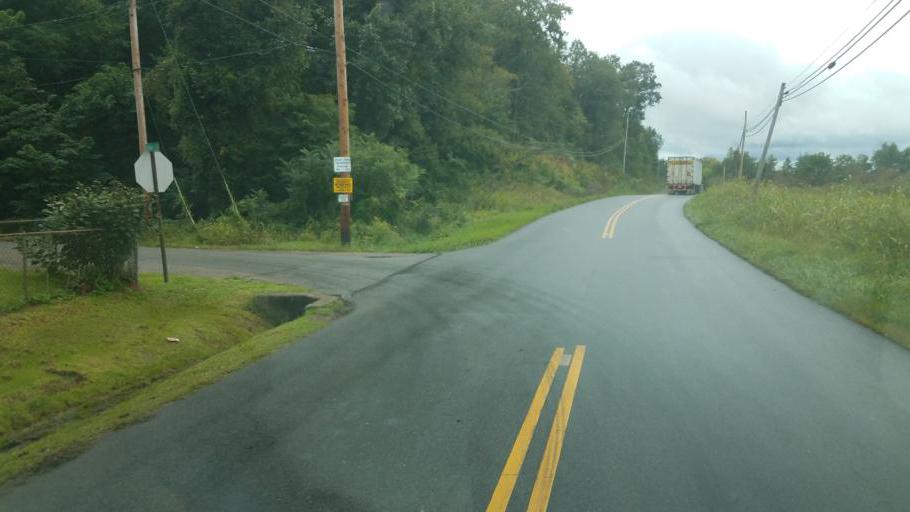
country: US
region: Ohio
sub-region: Scioto County
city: Wheelersburg
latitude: 38.6921
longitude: -82.8555
